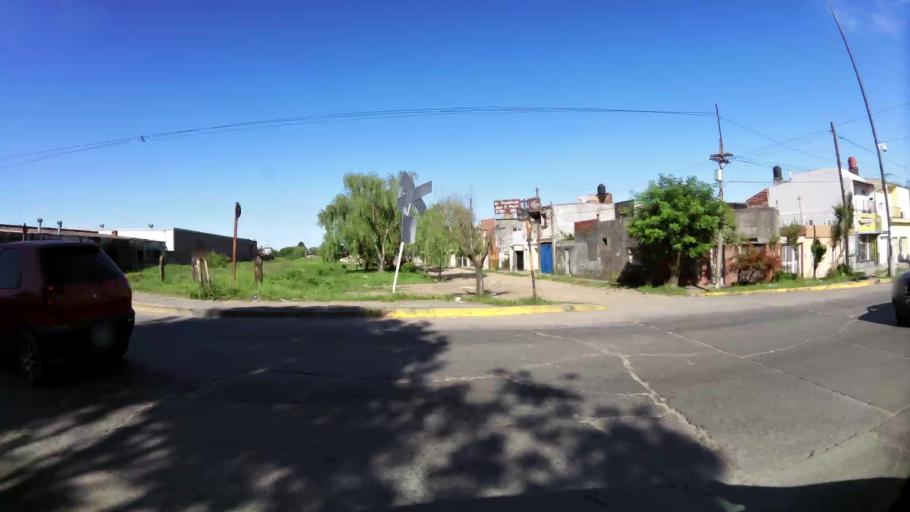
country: AR
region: Santa Fe
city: Santa Fe de la Vera Cruz
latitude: -31.6307
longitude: -60.7177
